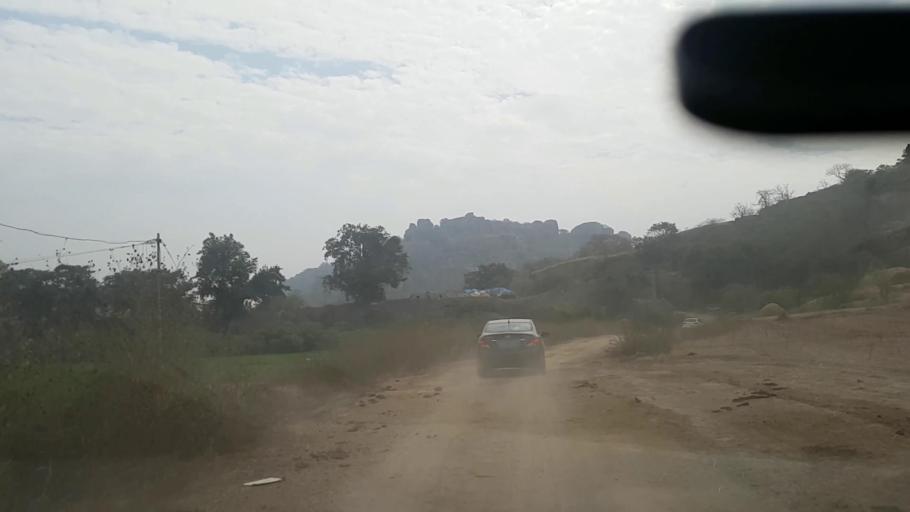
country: IN
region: Telangana
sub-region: Rangareddi
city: Lal Bahadur Nagar
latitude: 17.1812
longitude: 78.7963
